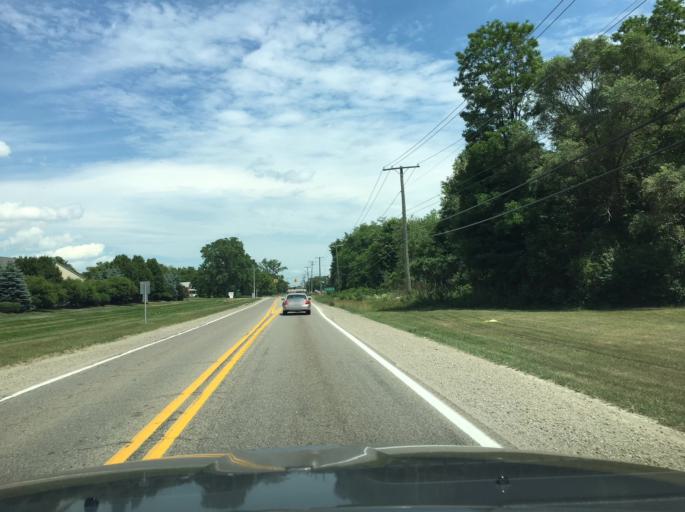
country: US
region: Michigan
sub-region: Macomb County
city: Shelby
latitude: 42.7147
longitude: -82.9990
